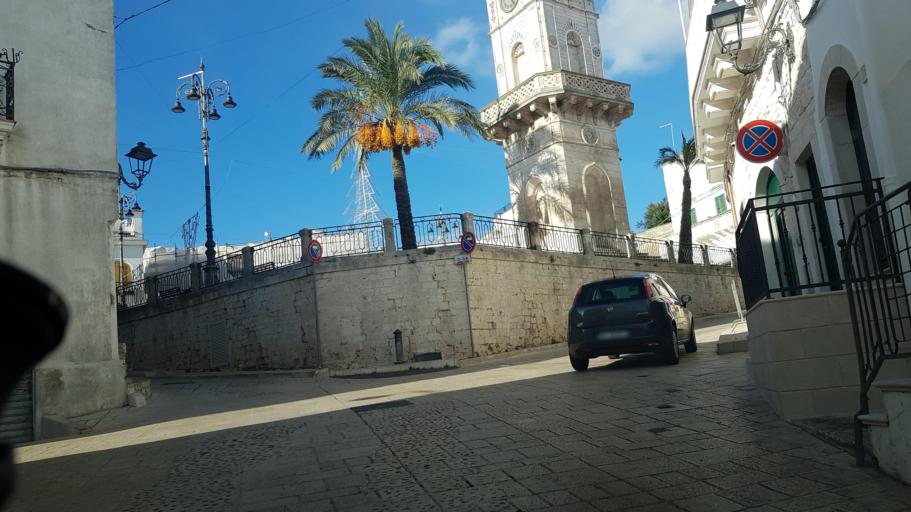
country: IT
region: Apulia
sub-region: Provincia di Brindisi
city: Ceglie Messapica
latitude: 40.6458
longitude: 17.5175
